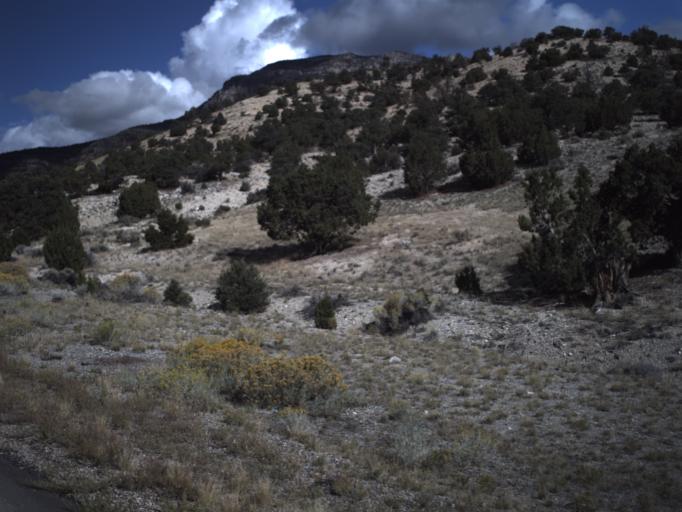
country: US
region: Utah
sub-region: Beaver County
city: Milford
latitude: 38.5139
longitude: -113.5327
